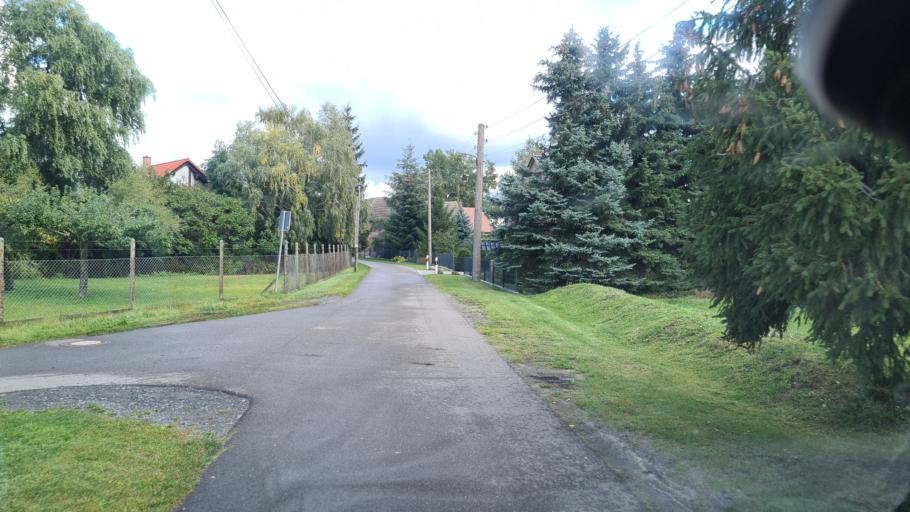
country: DE
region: Brandenburg
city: Grossraschen
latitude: 51.5802
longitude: 13.9548
